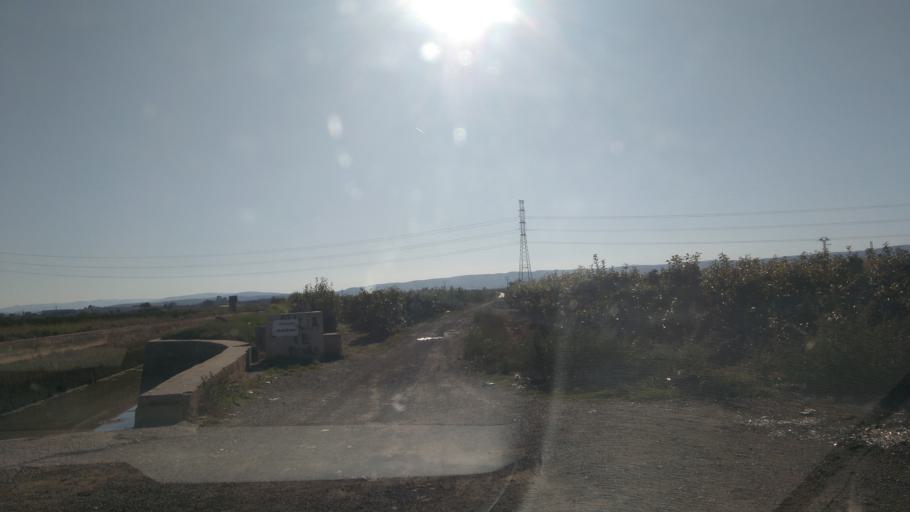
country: ES
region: Valencia
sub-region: Provincia de Valencia
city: L'Alcudia
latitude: 39.1867
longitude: -0.5191
